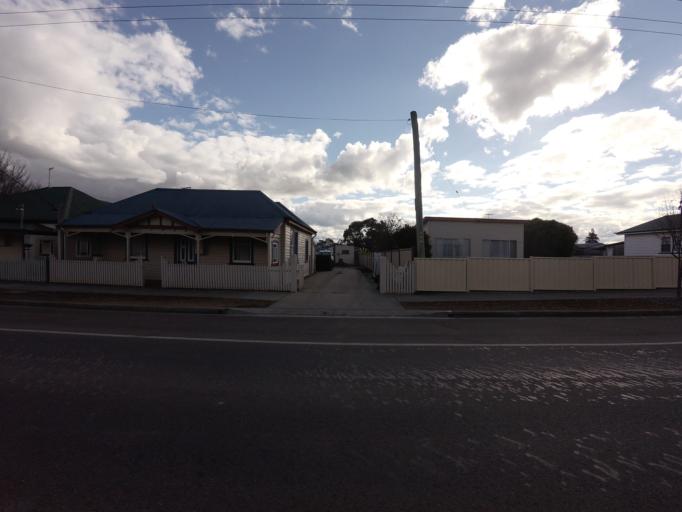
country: AU
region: Tasmania
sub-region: Northern Midlands
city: Longford
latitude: -41.6833
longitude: 147.0808
